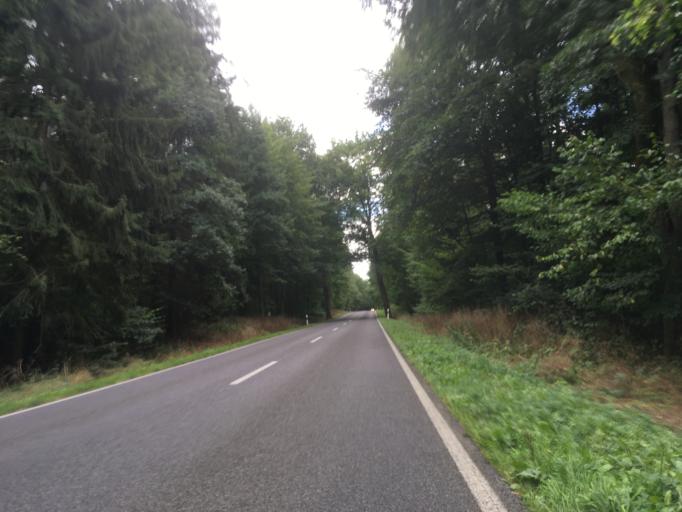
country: DE
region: Brandenburg
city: Gerswalde
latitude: 53.1990
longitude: 13.7154
